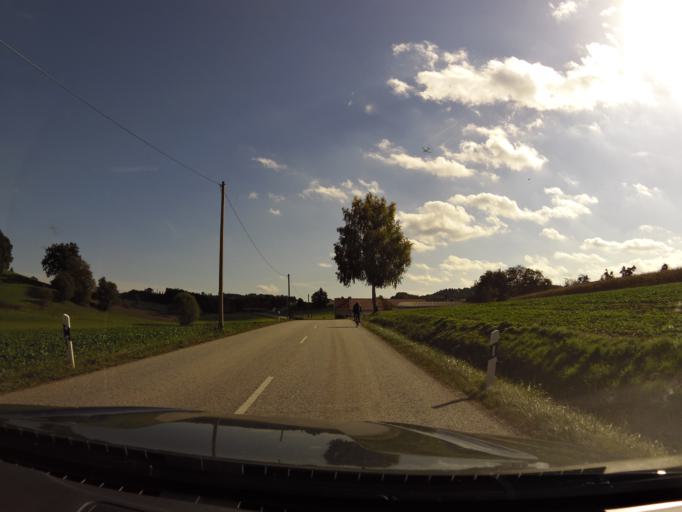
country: DE
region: Bavaria
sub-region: Lower Bavaria
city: Tiefenbach
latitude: 48.4845
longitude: 12.1103
